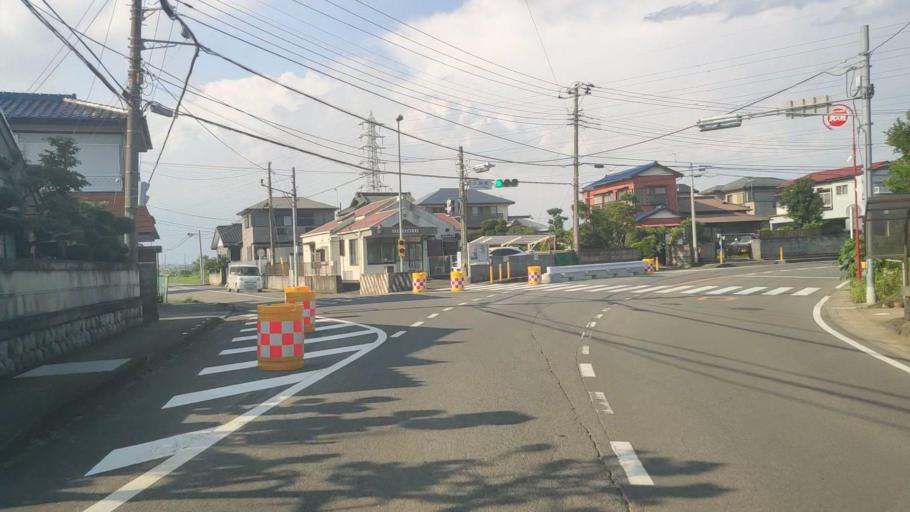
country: JP
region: Kanagawa
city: Isehara
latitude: 35.3714
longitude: 139.3283
